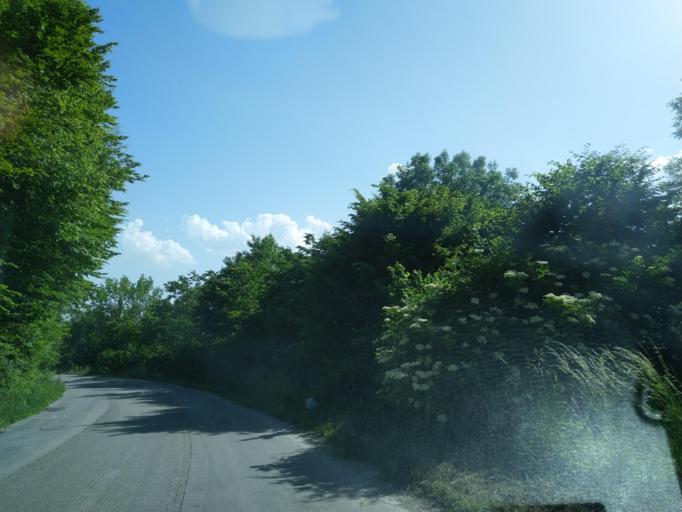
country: RS
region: Central Serbia
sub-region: Zlatiborski Okrug
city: Cajetina
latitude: 43.8698
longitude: 19.7135
